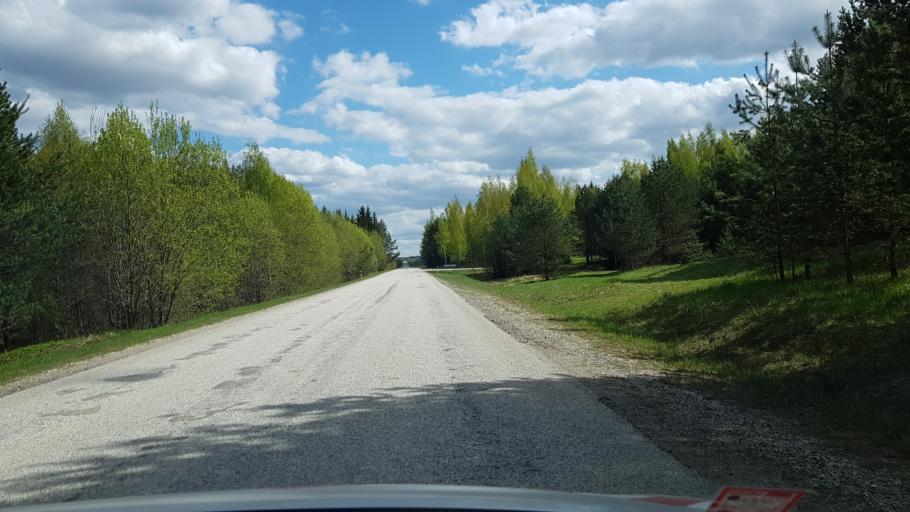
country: EE
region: Tartu
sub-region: UElenurme vald
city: Ulenurme
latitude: 58.2882
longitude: 26.8970
